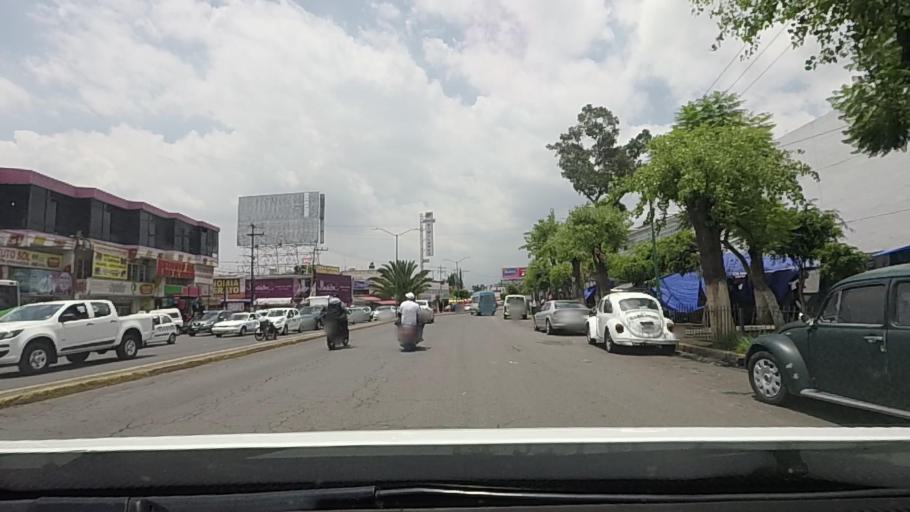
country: MX
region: Mexico
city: Chalco de Diaz Covarrubias
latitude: 19.2641
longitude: -98.8993
